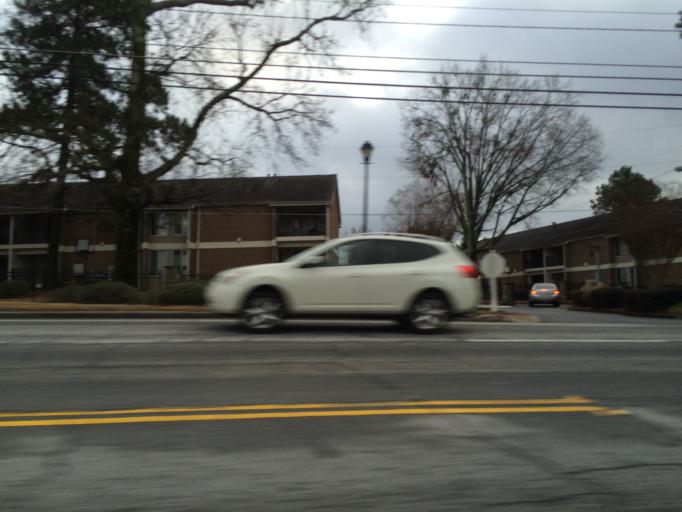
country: US
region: Georgia
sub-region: DeKalb County
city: Tucker
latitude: 33.8831
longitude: -84.2436
